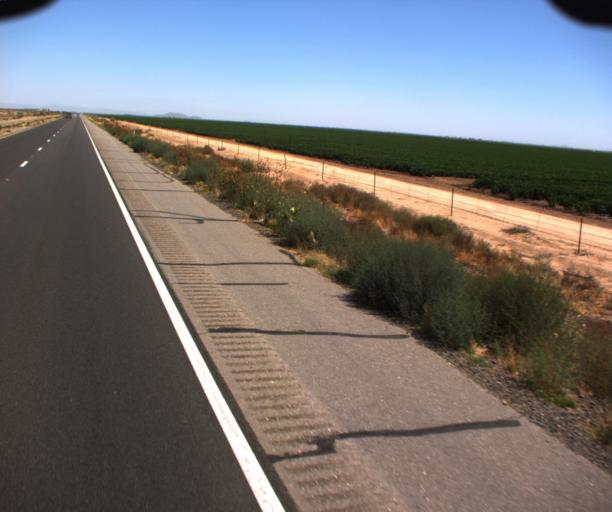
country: US
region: Arizona
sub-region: Pinal County
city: Maricopa
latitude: 32.9897
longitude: -112.0478
